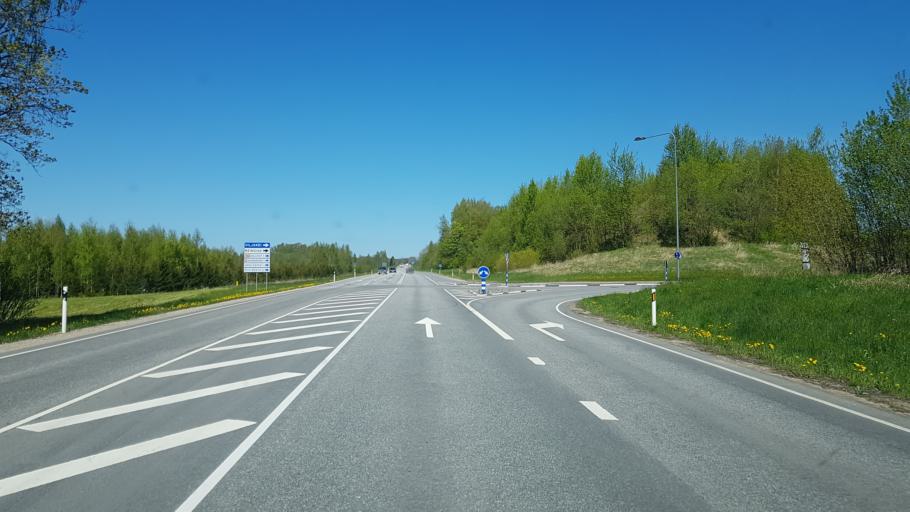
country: EE
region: Viljandimaa
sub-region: Viljandi linn
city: Viljandi
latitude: 58.3451
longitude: 25.5653
